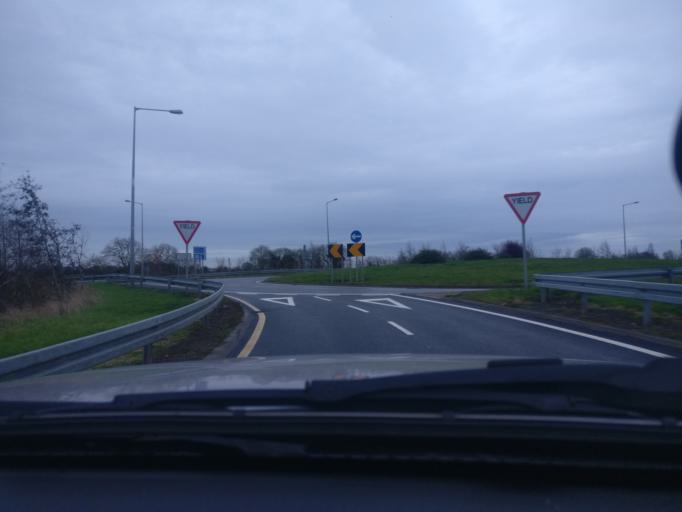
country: IE
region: Leinster
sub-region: An Mhi
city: Dunshaughlin
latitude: 53.5088
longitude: -6.5600
